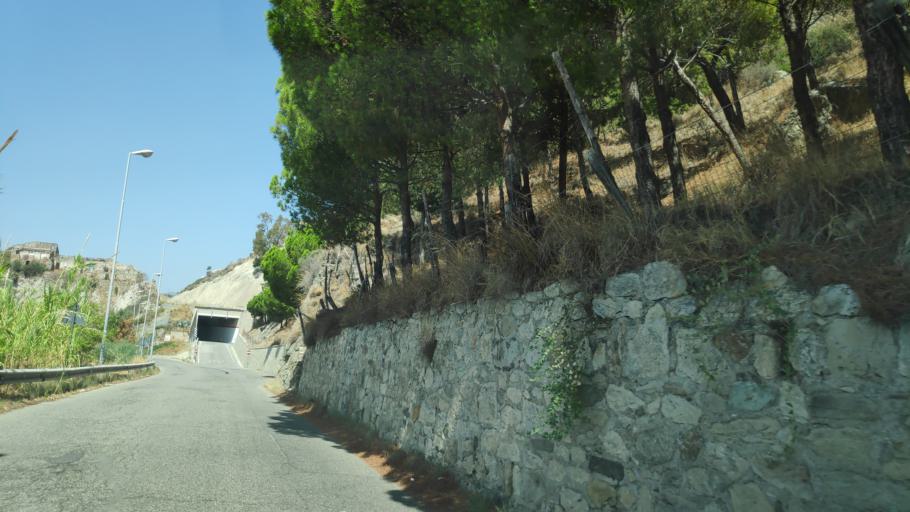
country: IT
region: Calabria
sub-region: Provincia di Reggio Calabria
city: Bova Marina
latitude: 37.9281
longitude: 15.9343
